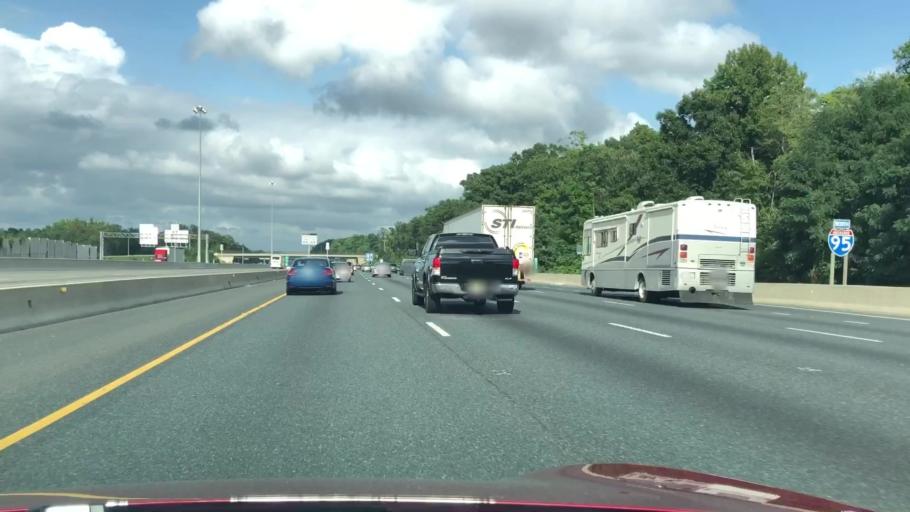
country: US
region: Maryland
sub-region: Baltimore County
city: Rossville
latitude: 39.3567
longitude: -76.4841
